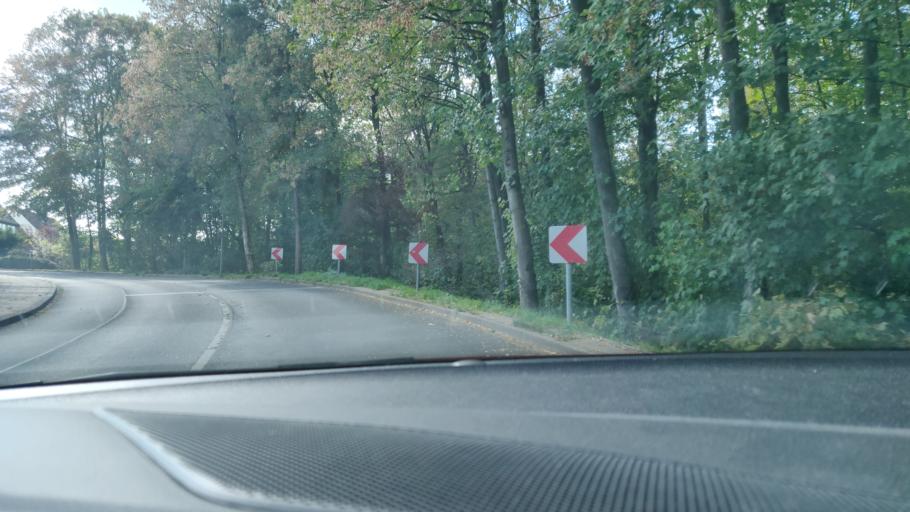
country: DE
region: North Rhine-Westphalia
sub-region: Regierungsbezirk Dusseldorf
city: Velbert
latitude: 51.3575
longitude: 7.0335
